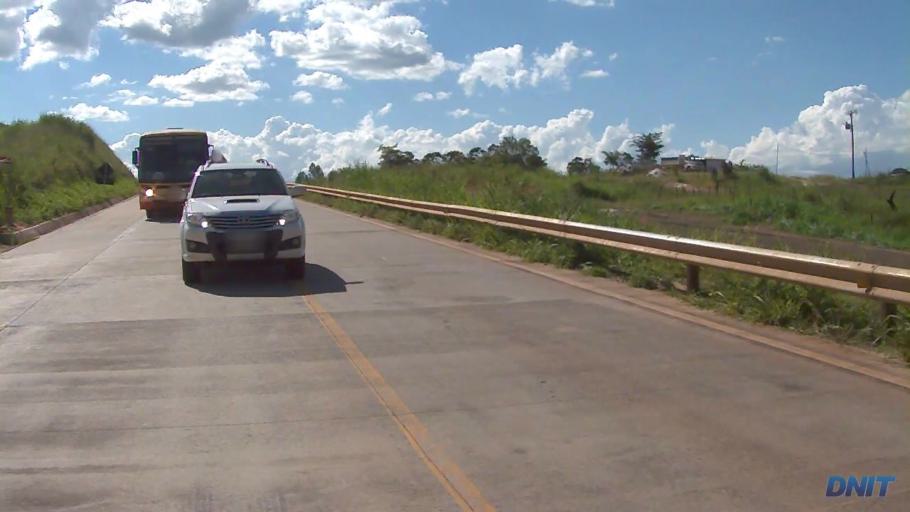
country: BR
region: Minas Gerais
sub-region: Barao De Cocais
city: Barao de Cocais
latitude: -19.7805
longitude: -43.4376
